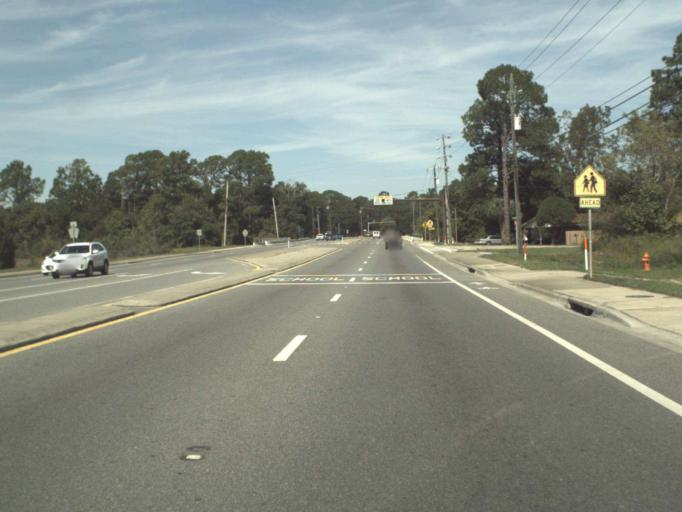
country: US
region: Florida
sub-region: Bay County
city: Lynn Haven
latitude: 30.2868
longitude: -85.6383
